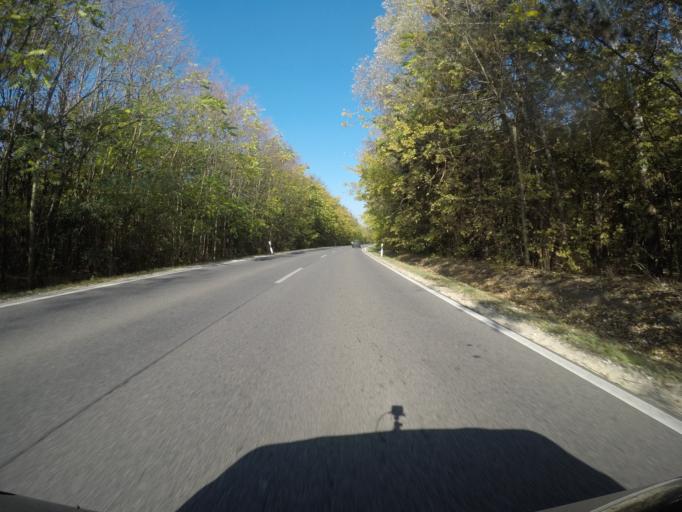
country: HU
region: Tolna
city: Tengelic
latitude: 46.5392
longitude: 18.6531
